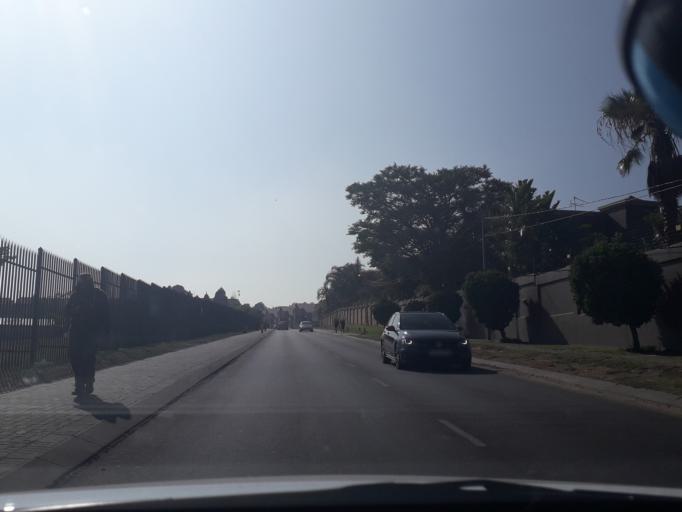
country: ZA
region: Gauteng
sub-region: City of Johannesburg Metropolitan Municipality
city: Diepsloot
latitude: -26.0455
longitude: 27.9676
